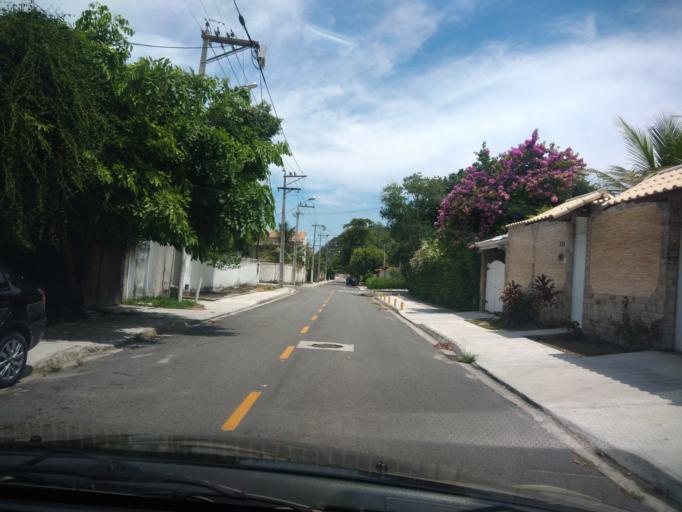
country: BR
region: Rio de Janeiro
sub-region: Niteroi
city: Niteroi
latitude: -22.9319
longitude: -43.0741
